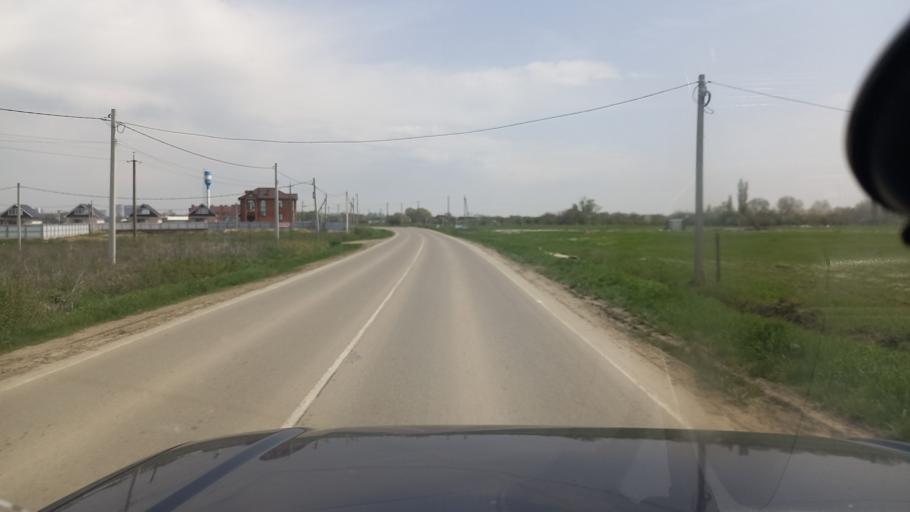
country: RU
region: Adygeya
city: Yablonovskiy
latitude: 44.9868
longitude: 38.9865
